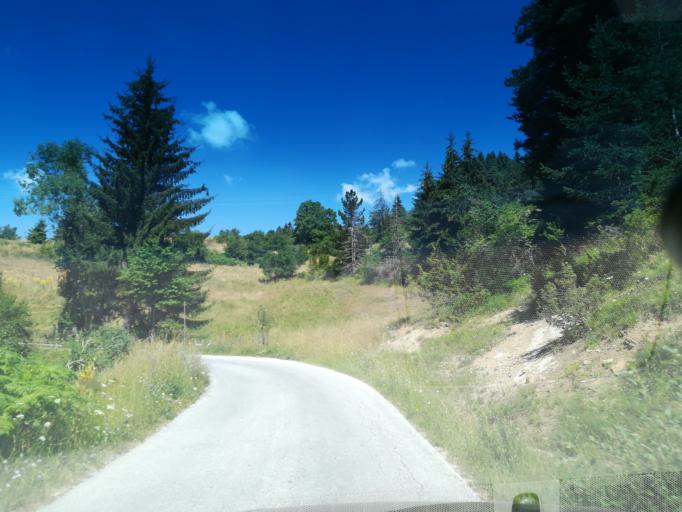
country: BG
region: Smolyan
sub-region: Obshtina Chepelare
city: Chepelare
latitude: 41.6700
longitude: 24.7861
